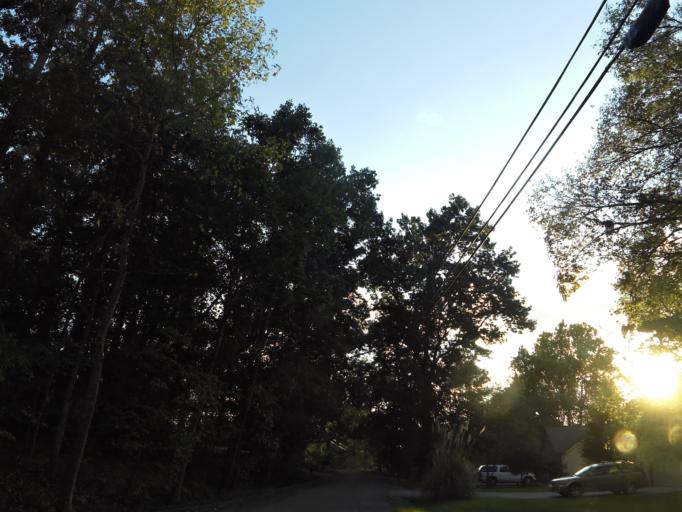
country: US
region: Tennessee
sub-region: Knox County
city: Knoxville
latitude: 35.9166
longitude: -83.9503
